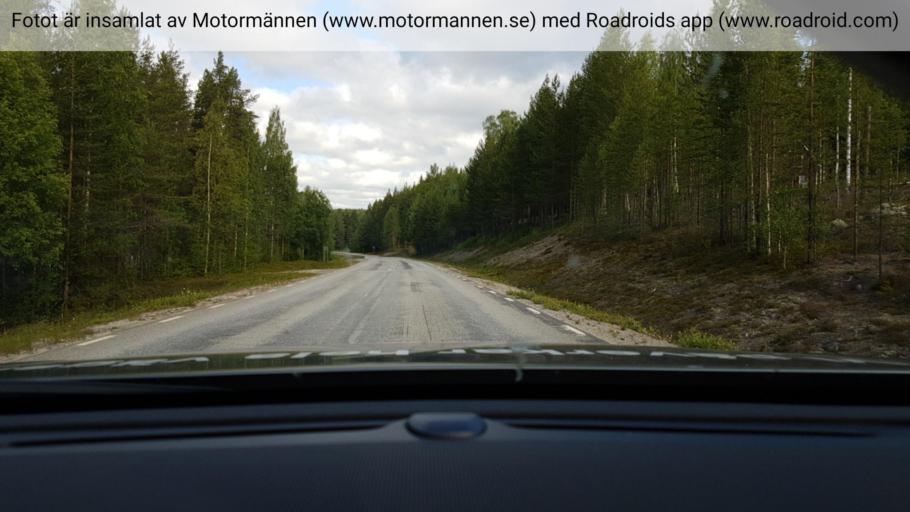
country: SE
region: Vaesterbotten
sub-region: Lycksele Kommun
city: Lycksele
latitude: 64.8483
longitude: 18.7605
